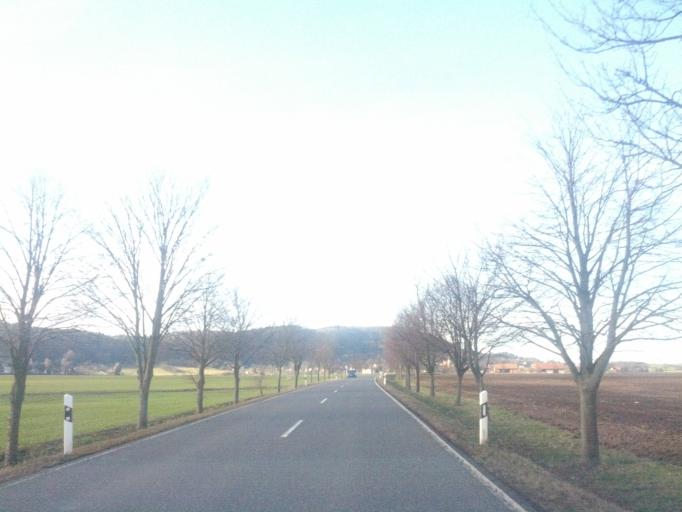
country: DE
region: Thuringia
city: Seebergen
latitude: 50.9137
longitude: 10.8151
